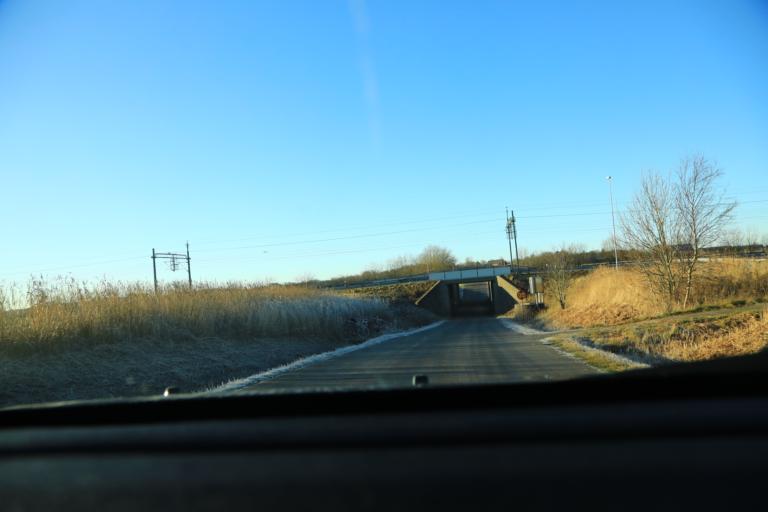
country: SE
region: Halland
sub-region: Varbergs Kommun
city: Varberg
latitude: 57.2056
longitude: 12.2234
